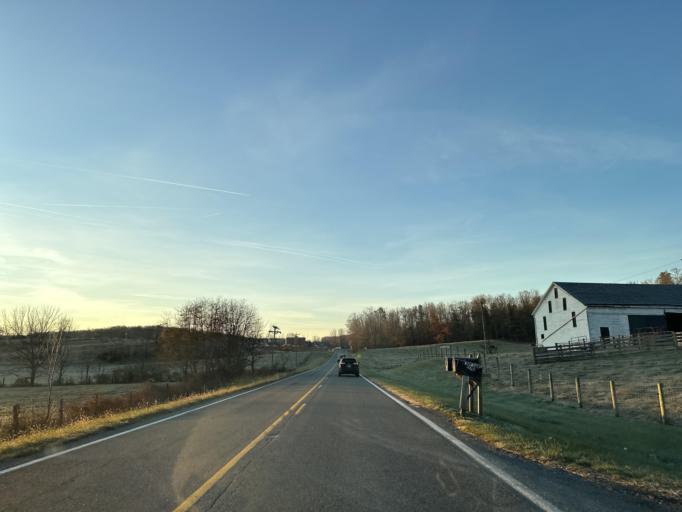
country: US
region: Virginia
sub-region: City of Staunton
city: Staunton
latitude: 38.1994
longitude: -79.2193
